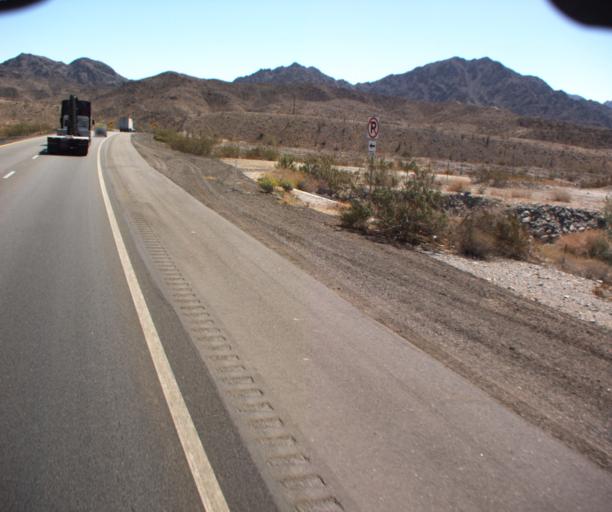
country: US
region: Arizona
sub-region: Yuma County
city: Fortuna Foothills
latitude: 32.6599
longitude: -114.3498
